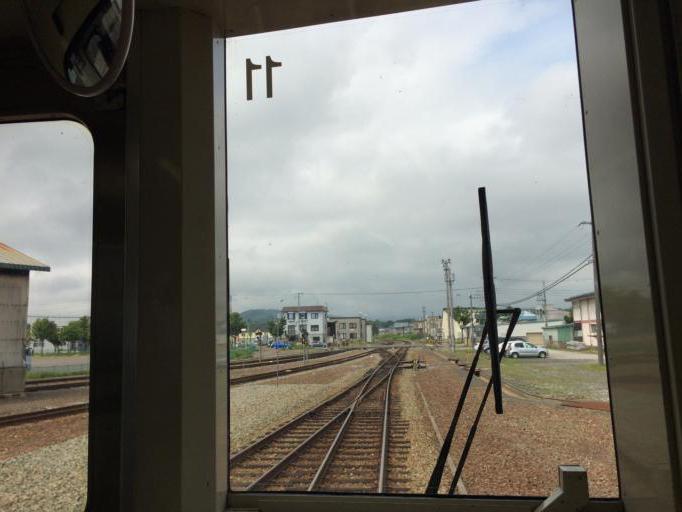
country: JP
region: Hokkaido
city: Niseko Town
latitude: 42.9033
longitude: 140.7456
